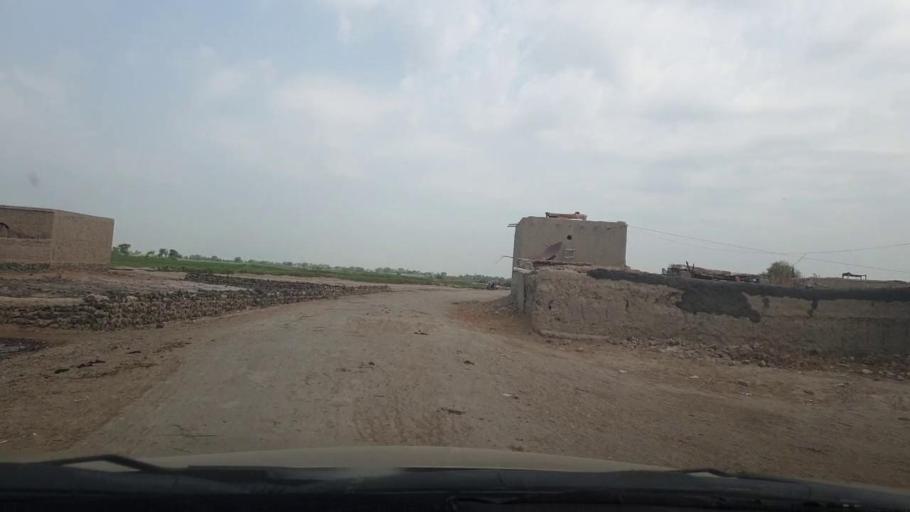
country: PK
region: Sindh
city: Ratodero
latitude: 27.7031
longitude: 68.2290
